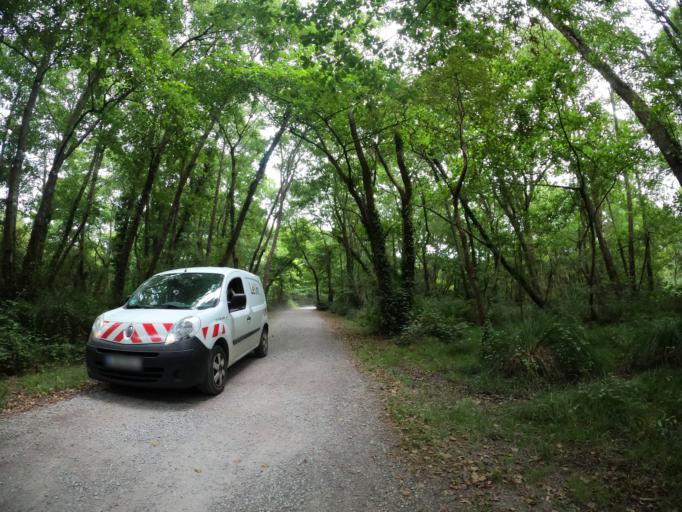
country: FR
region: Aquitaine
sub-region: Departement des Landes
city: Leon
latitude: 43.8869
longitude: -1.3089
